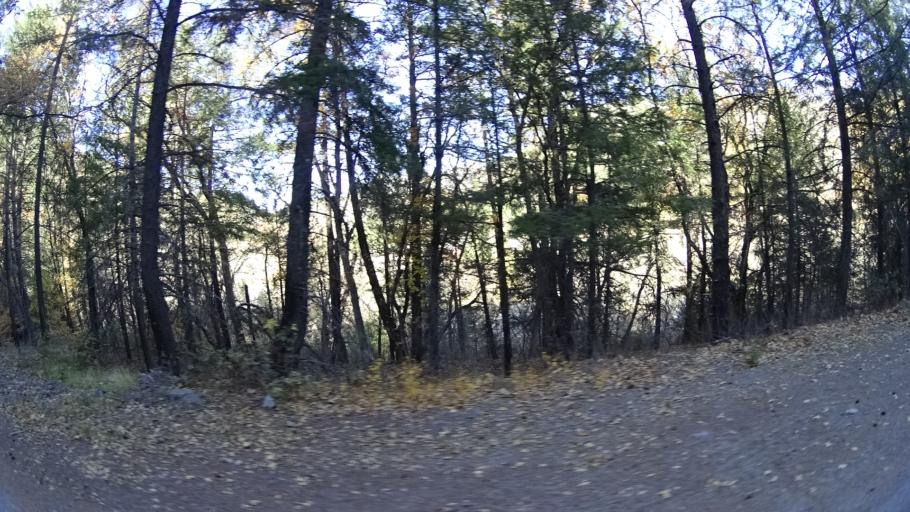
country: US
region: California
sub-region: Siskiyou County
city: Yreka
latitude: 41.8472
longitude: -122.6917
